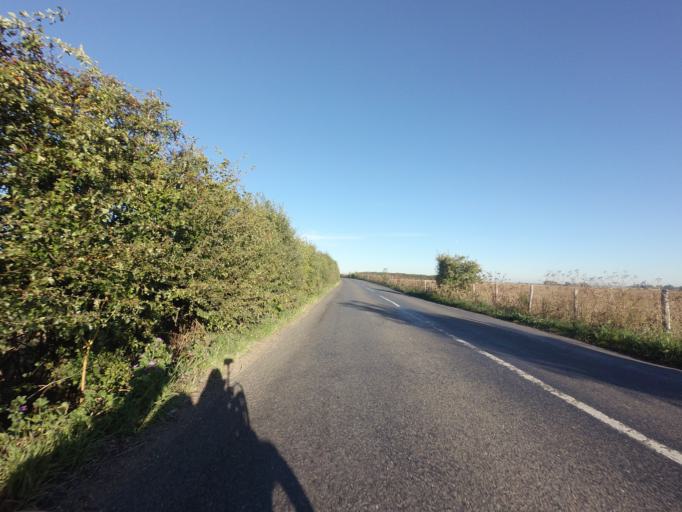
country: GB
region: England
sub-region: Kent
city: Herne Bay
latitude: 51.3526
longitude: 1.1682
